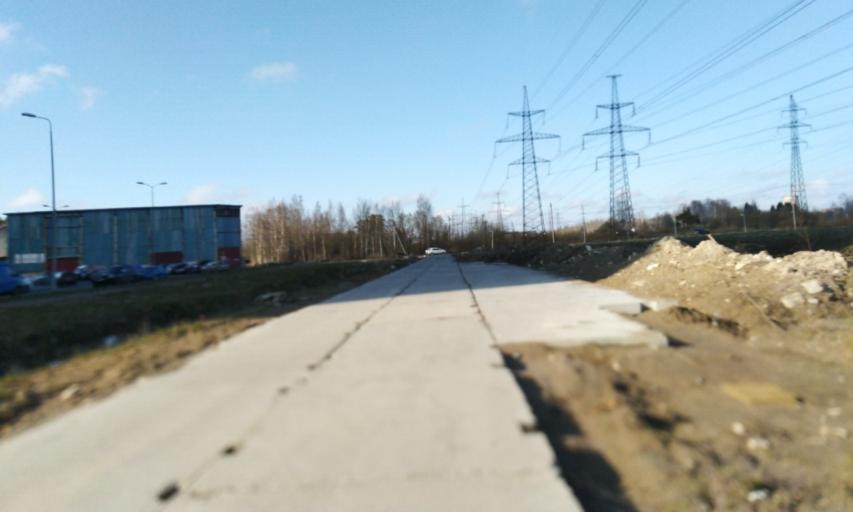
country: RU
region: Leningrad
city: Murino
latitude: 60.0692
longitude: 30.4510
